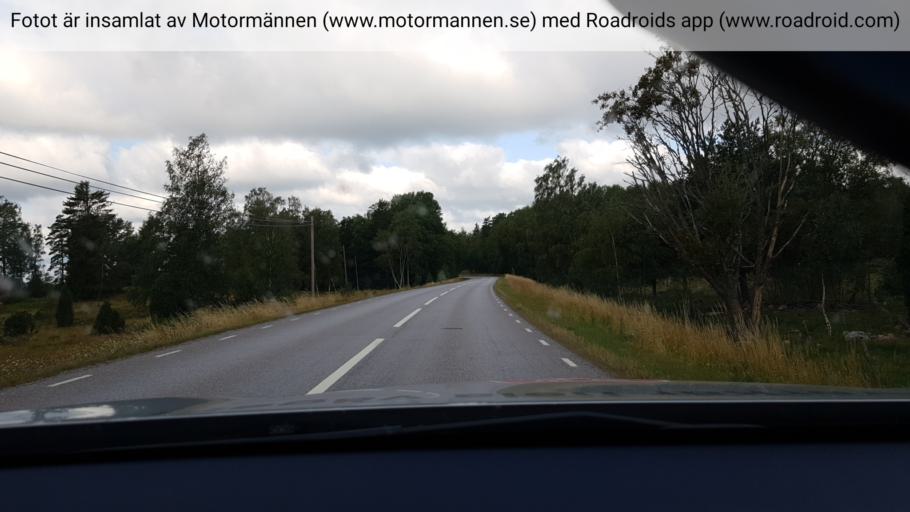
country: SE
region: Stockholm
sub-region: Norrtalje Kommun
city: Nykvarn
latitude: 59.9097
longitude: 18.2856
